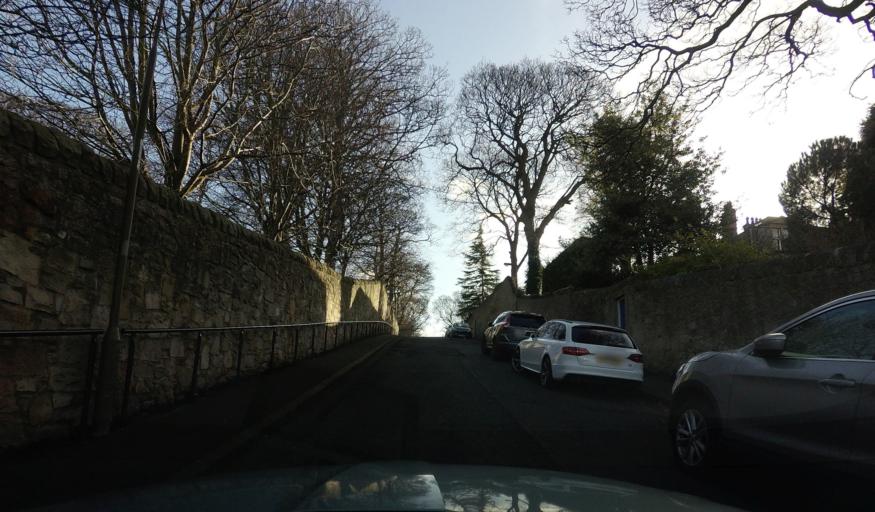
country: GB
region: Scotland
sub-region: Edinburgh
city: Edinburgh
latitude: 55.9794
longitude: -3.2017
